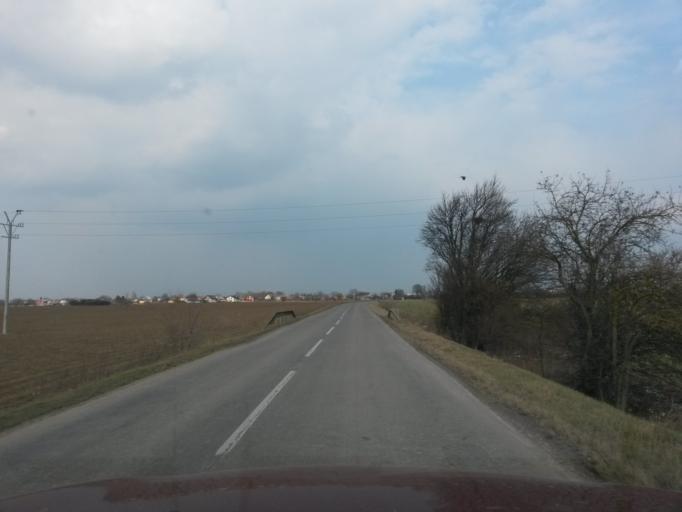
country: SK
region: Kosicky
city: Kosice
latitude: 48.6131
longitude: 21.2444
